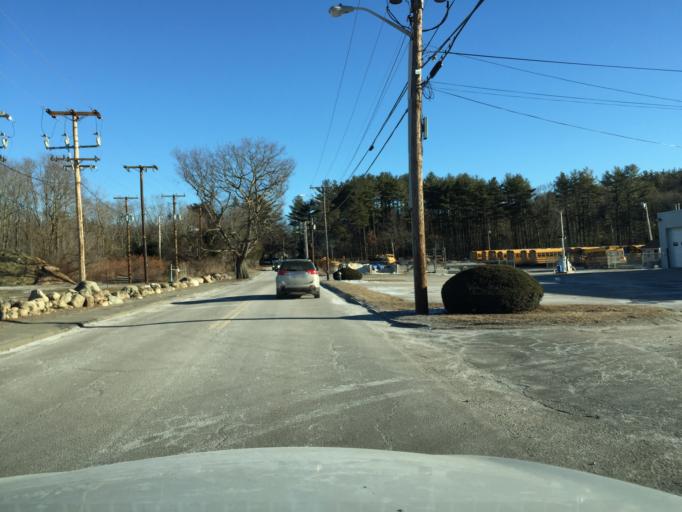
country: US
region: Massachusetts
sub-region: Norfolk County
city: Foxborough
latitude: 42.0549
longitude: -71.2383
